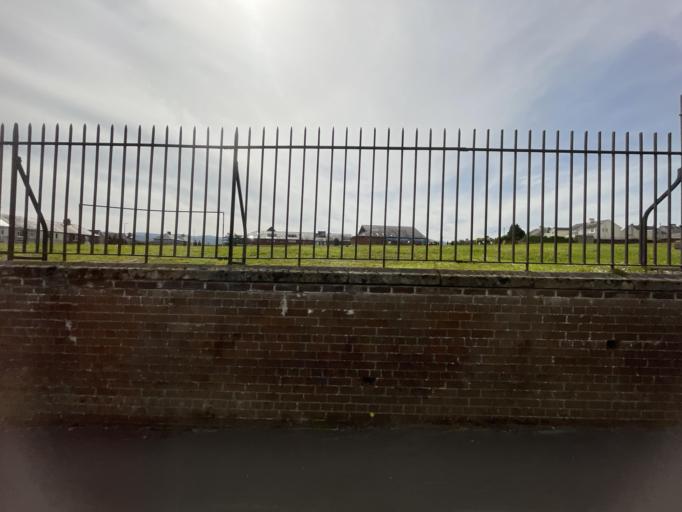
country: GB
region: Wales
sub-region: Gwynedd
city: Bangor
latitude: 53.2213
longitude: -4.1467
